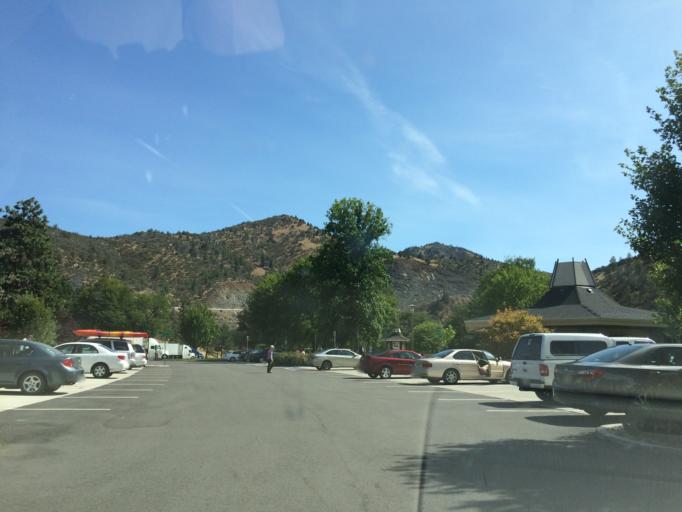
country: US
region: California
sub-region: Siskiyou County
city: Montague
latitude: 41.8537
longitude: -122.5727
